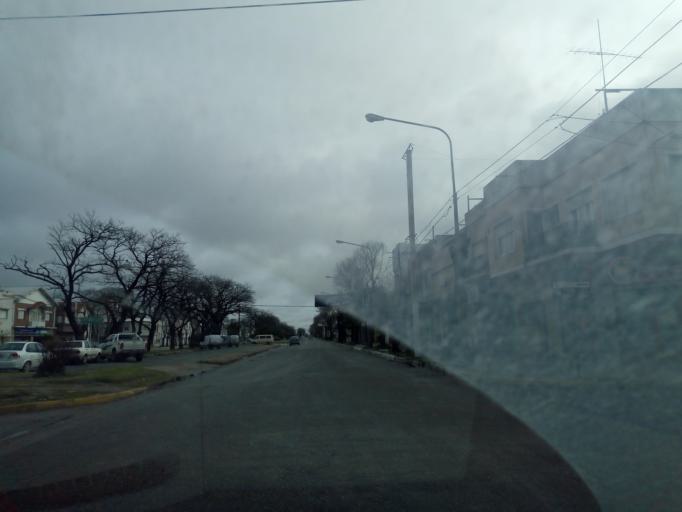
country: AR
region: Buenos Aires
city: Necochea
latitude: -38.5584
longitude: -58.7341
